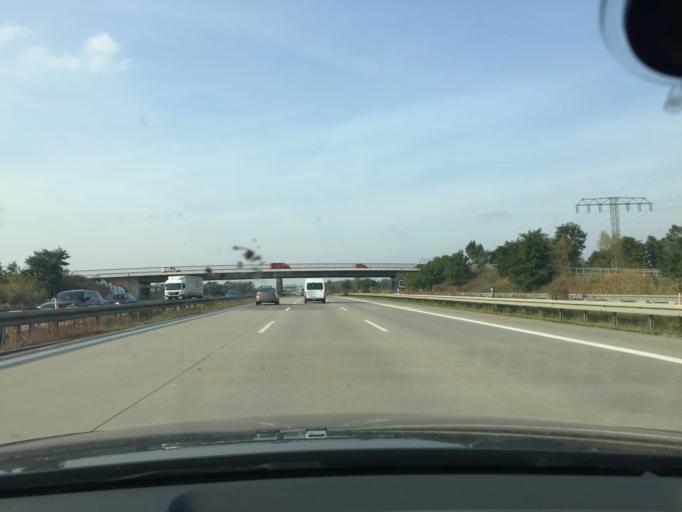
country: DE
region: Brandenburg
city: Petershagen
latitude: 52.5007
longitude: 13.7471
